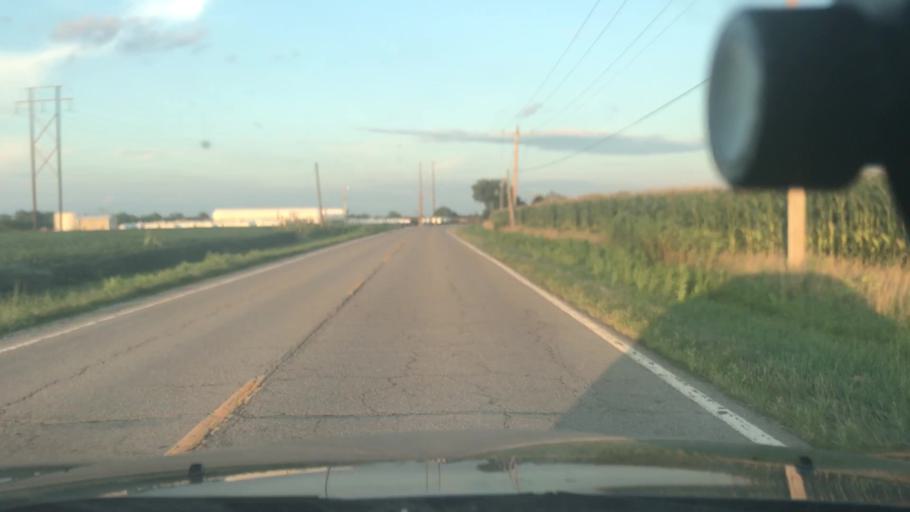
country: US
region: Illinois
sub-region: Washington County
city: Okawville
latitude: 38.4183
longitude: -89.5448
